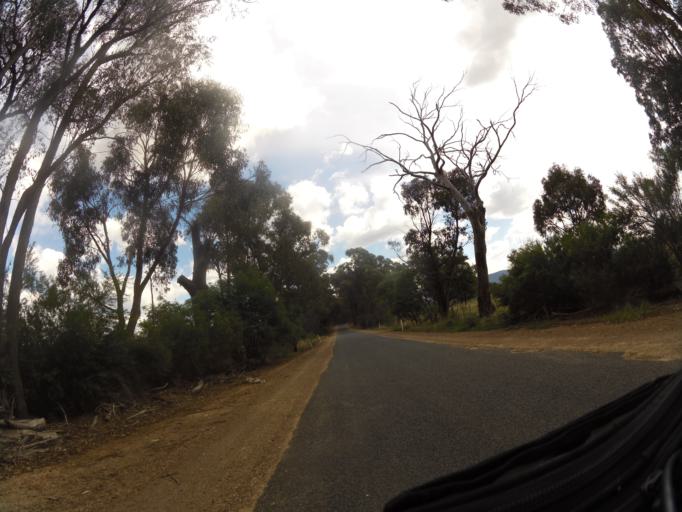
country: AU
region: Victoria
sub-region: Benalla
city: Benalla
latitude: -36.7497
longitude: 145.9976
